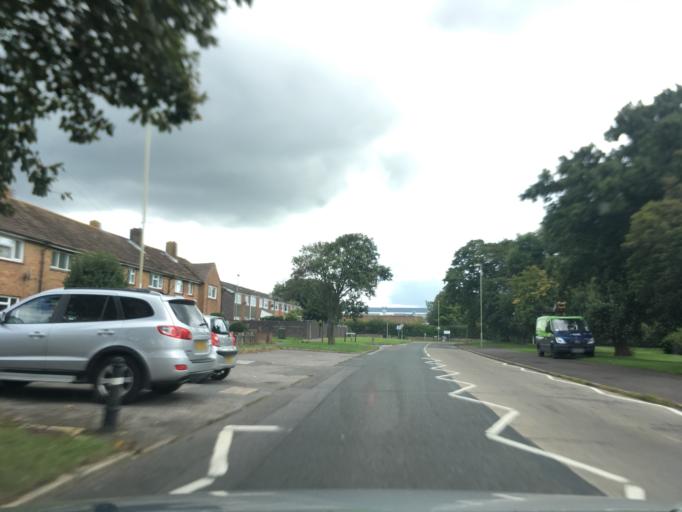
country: GB
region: England
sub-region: Hampshire
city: Havant
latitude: 50.8600
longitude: -0.9749
